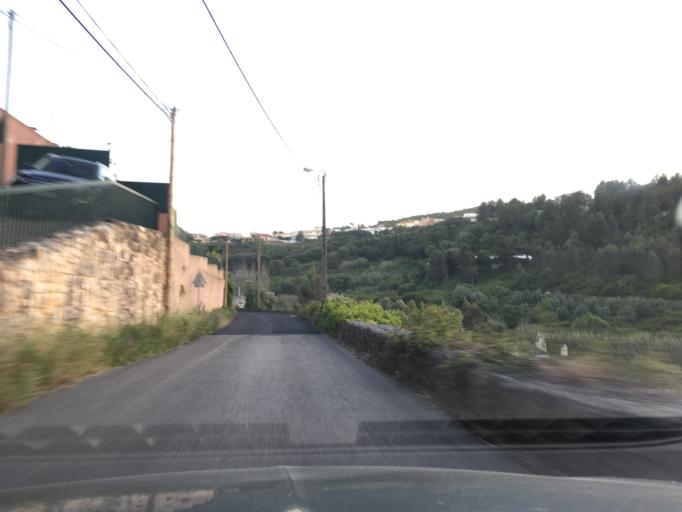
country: PT
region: Lisbon
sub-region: Oeiras
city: Quejas
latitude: 38.7216
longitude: -9.2759
